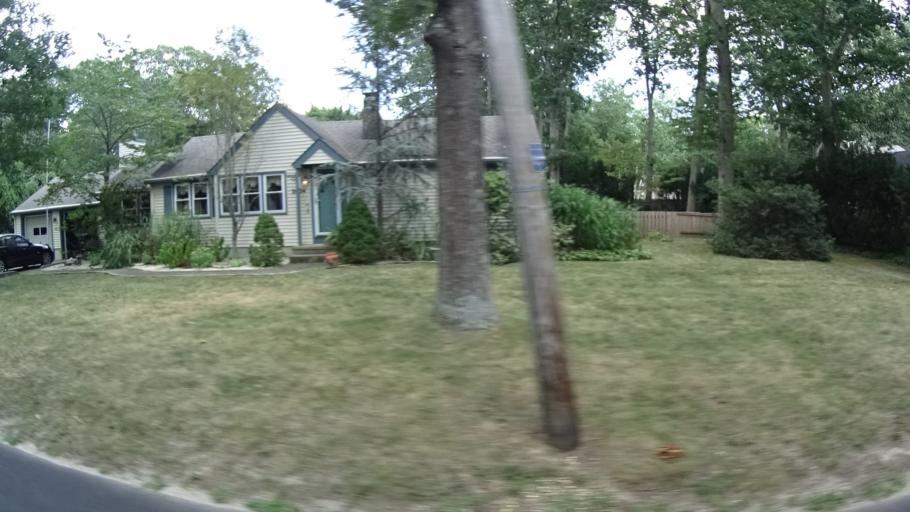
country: US
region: New Jersey
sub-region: Monmouth County
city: Brielle
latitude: 40.1063
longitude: -74.0851
